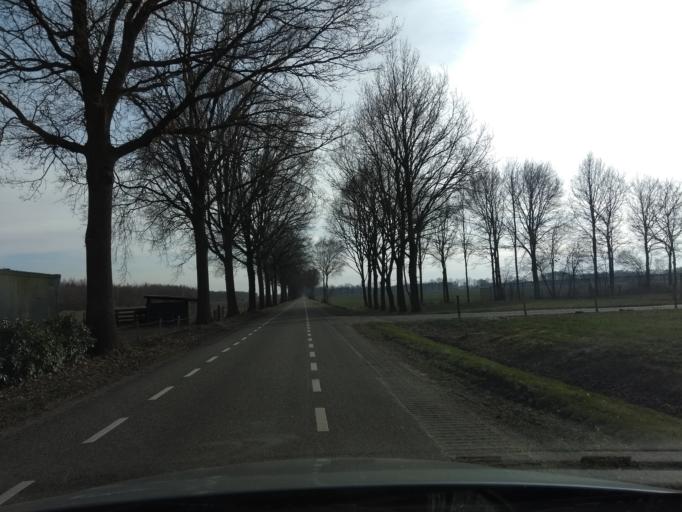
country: NL
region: Overijssel
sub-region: Gemeente Twenterand
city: Westerhaar-Vriezenveensewijk
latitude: 52.4572
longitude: 6.6528
